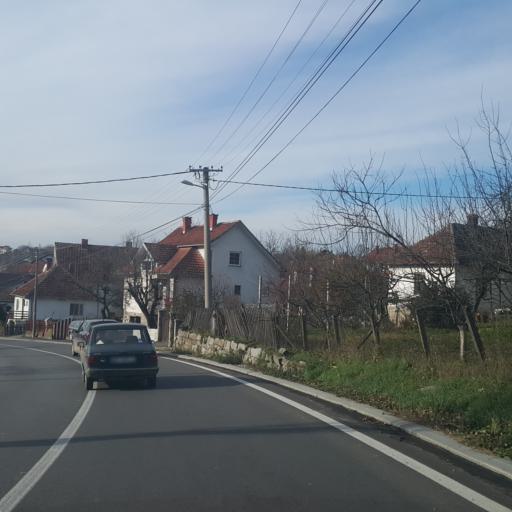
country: RS
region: Central Serbia
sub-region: Sumadijski Okrug
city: Arangelovac
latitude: 44.3350
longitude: 20.4647
